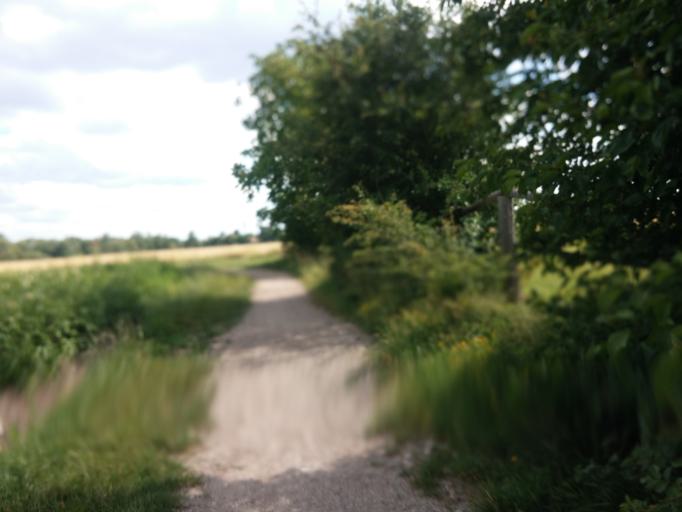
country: DE
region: Bavaria
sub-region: Upper Bavaria
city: Unterfoehring
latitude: 48.1515
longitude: 11.6625
